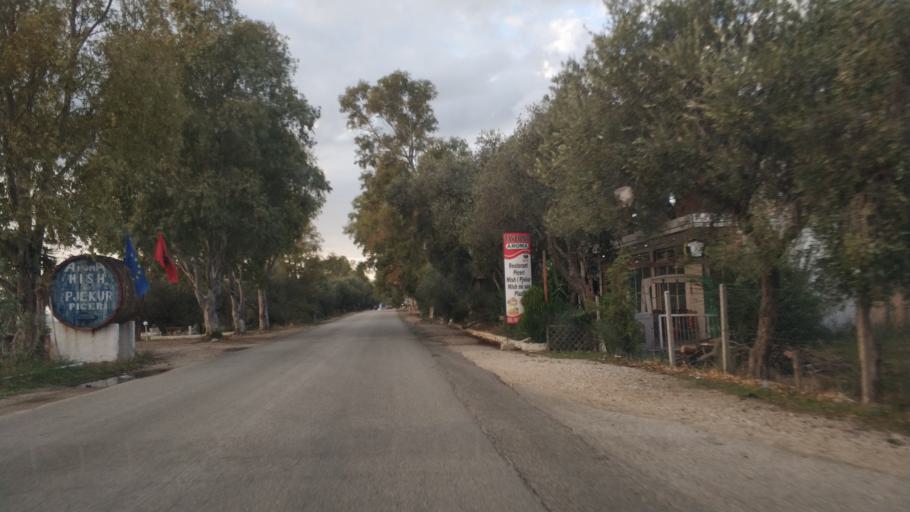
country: AL
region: Vlore
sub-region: Rrethi i Vlores
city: Orikum
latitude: 40.3585
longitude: 19.4824
